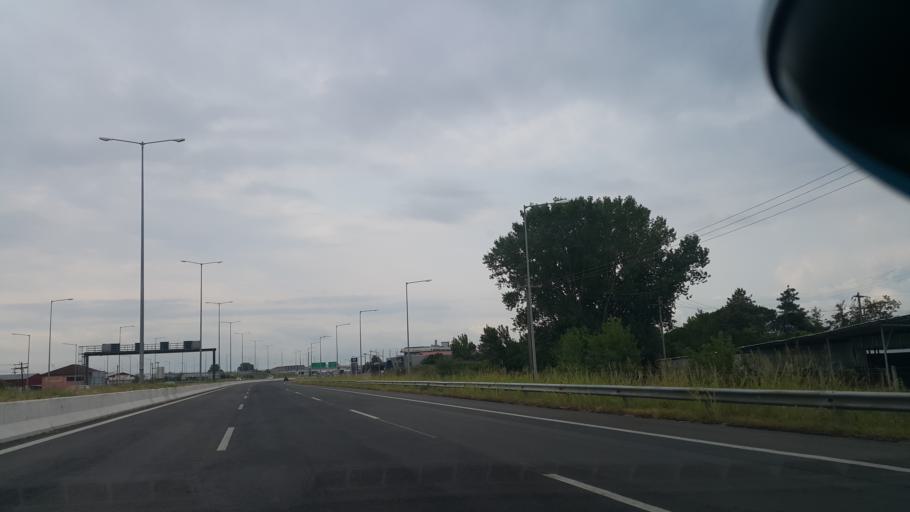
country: GR
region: Central Macedonia
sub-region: Nomos Pierias
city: Peristasi
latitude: 40.2611
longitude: 22.5292
